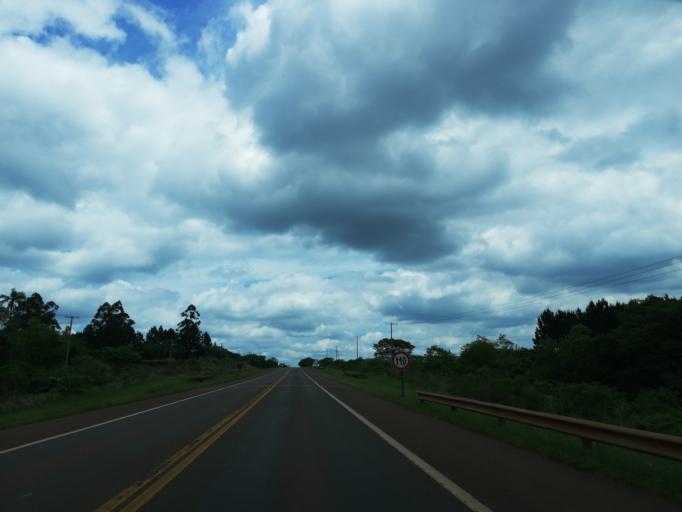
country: AR
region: Misiones
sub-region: Departamento de Leandro N. Alem
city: Leandro N. Alem
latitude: -27.6302
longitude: -55.3410
